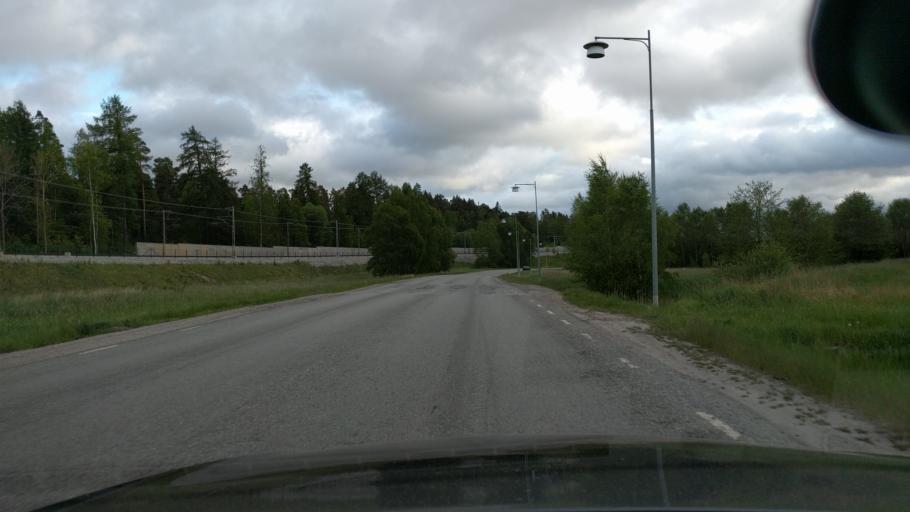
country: SE
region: Stockholm
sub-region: Vallentuna Kommun
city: Vallentuna
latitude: 59.5296
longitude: 18.0762
